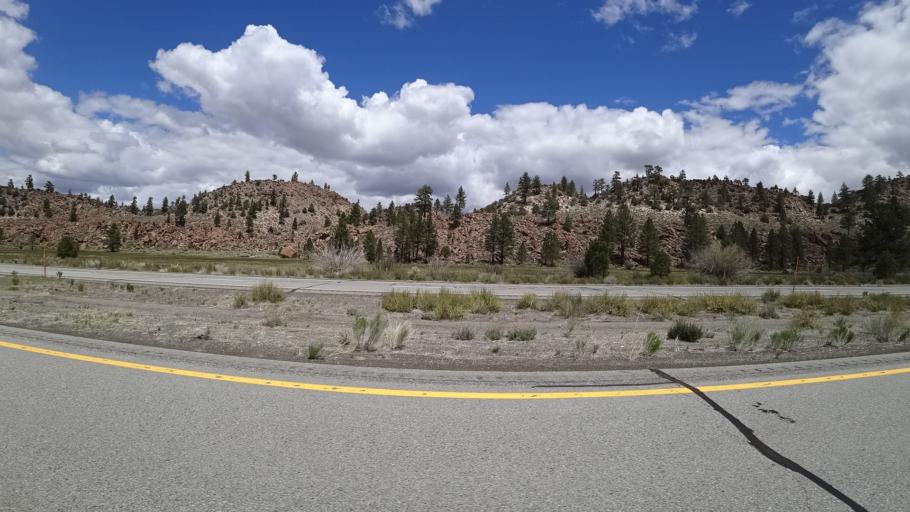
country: US
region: California
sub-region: Mono County
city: Mammoth Lakes
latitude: 37.5677
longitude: -118.6912
